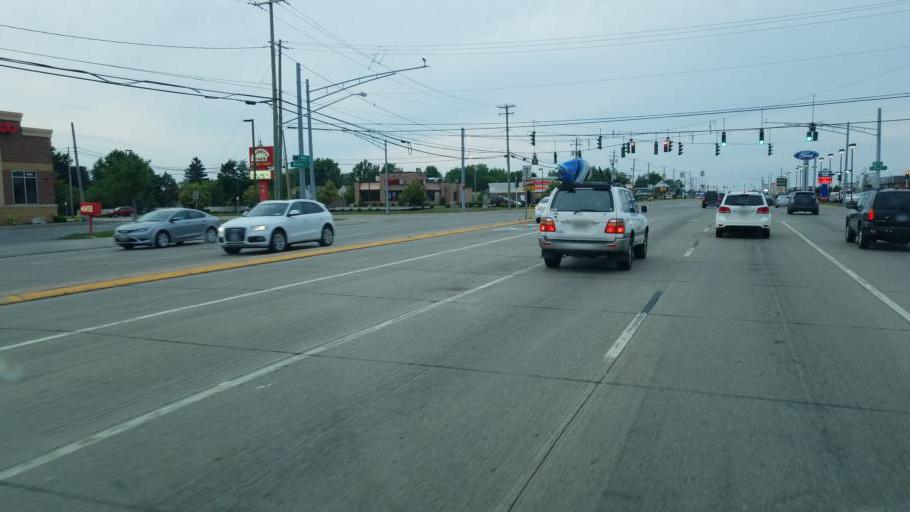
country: US
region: New York
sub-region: Erie County
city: Harris Hill
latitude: 42.9558
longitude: -78.6968
